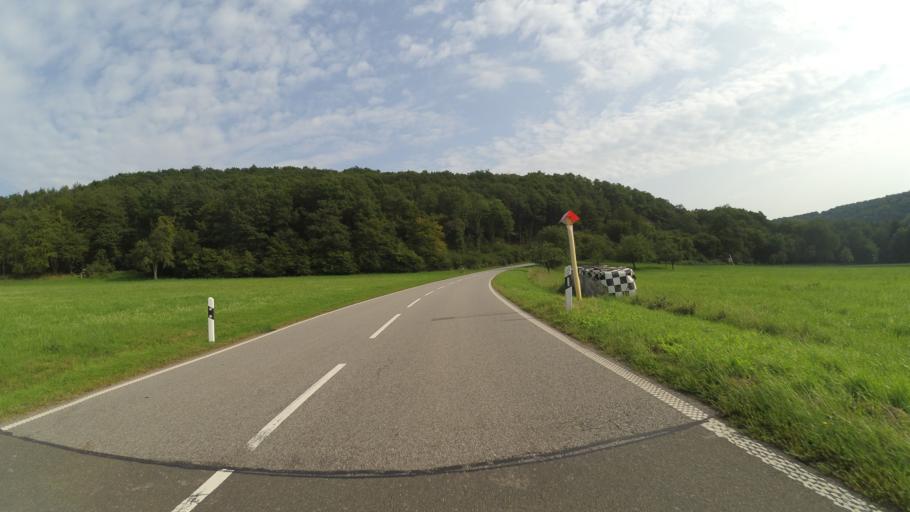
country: DE
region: Rheinland-Pfalz
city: Irsch
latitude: 49.5984
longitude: 6.5946
